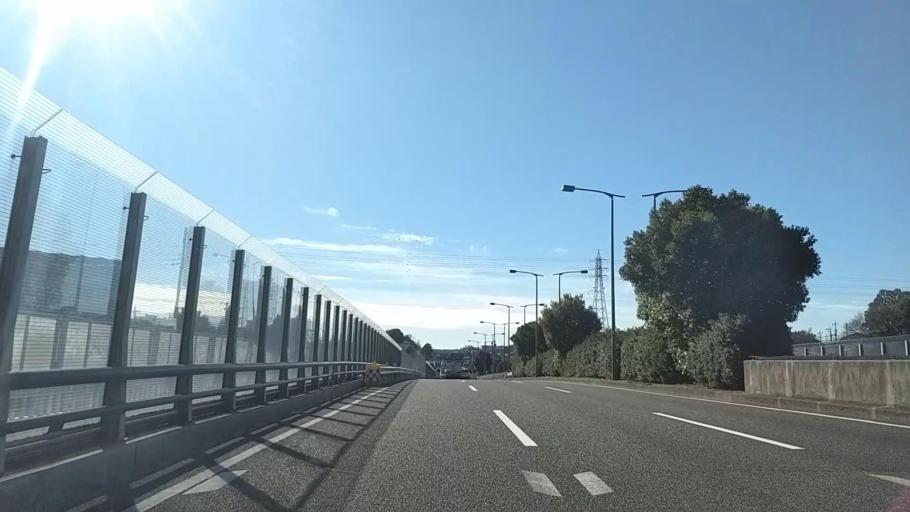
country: JP
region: Kanagawa
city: Yokohama
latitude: 35.4664
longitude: 139.5654
